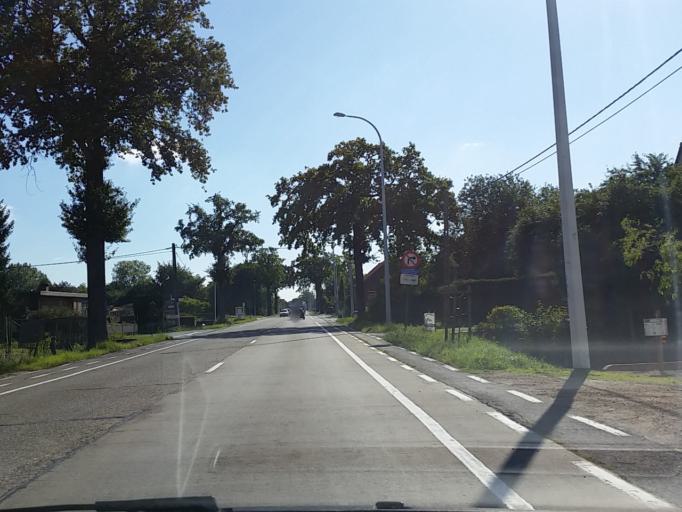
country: BE
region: Flanders
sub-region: Provincie Vlaams-Brabant
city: Haacht
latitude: 50.9348
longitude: 4.6256
